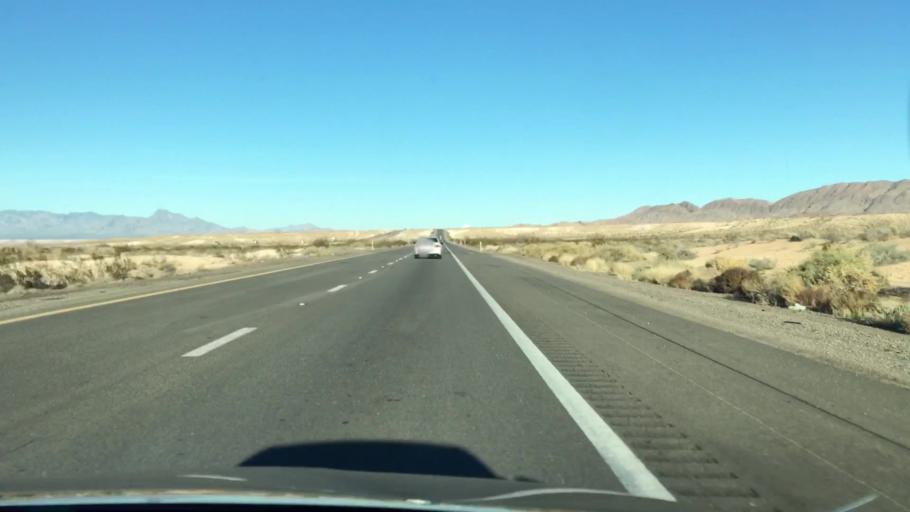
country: US
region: Nevada
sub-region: Clark County
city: Moapa Town
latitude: 36.5597
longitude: -114.6853
